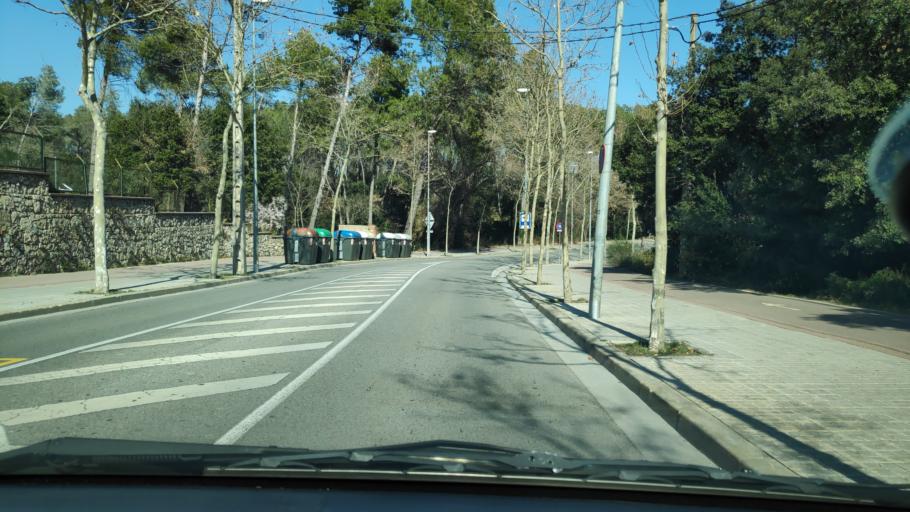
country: ES
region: Catalonia
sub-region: Provincia de Barcelona
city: Sant Quirze del Valles
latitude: 41.5541
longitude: 2.0688
